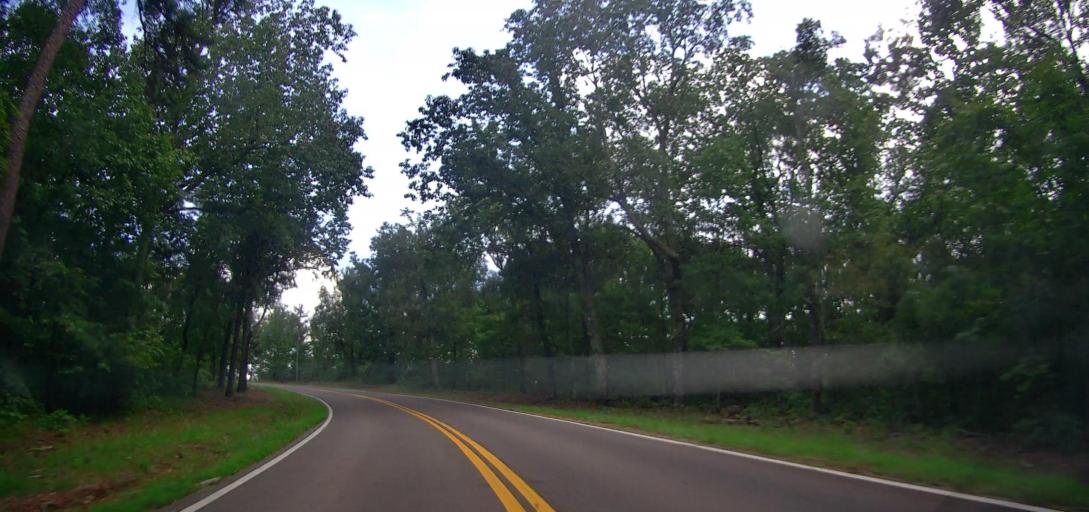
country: US
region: Georgia
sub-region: Harris County
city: Pine Mountain
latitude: 32.8471
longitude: -84.7821
